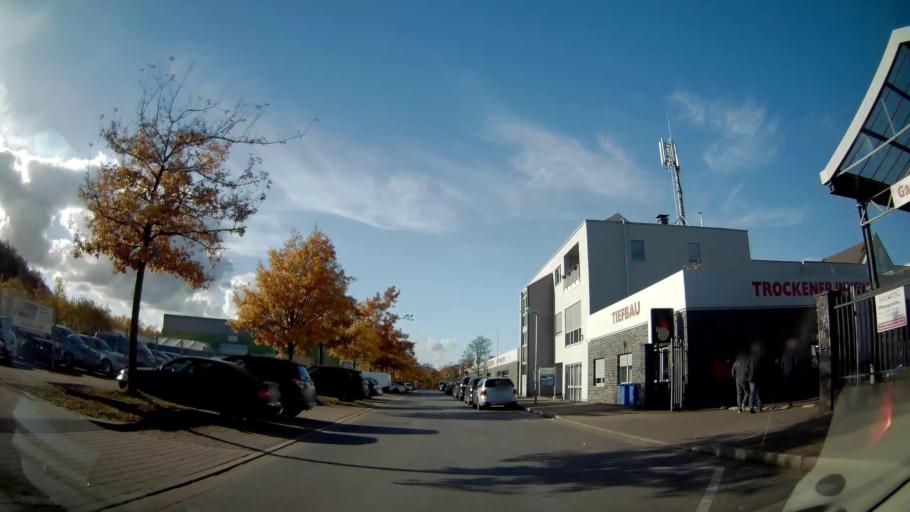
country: DE
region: North Rhine-Westphalia
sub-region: Regierungsbezirk Munster
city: Gladbeck
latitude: 51.5547
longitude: 6.9876
